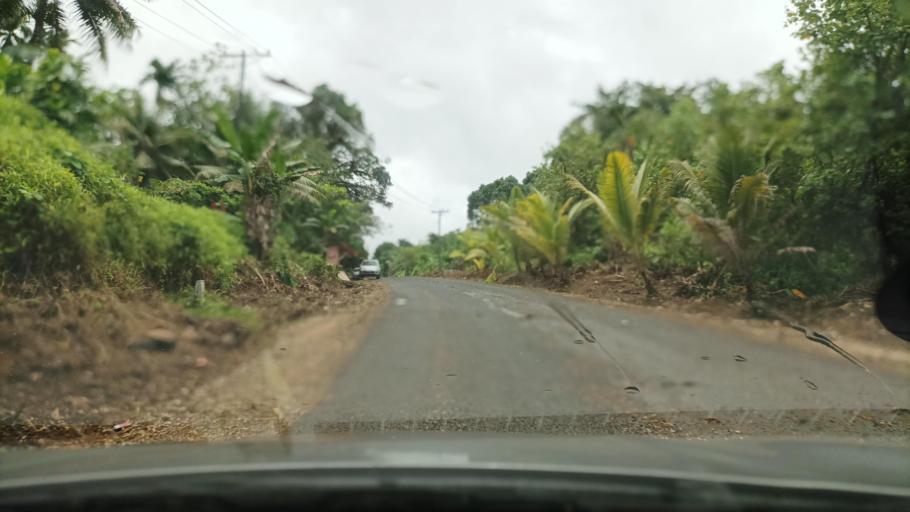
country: FM
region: Pohnpei
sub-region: Madolenihm Municipality
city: Madolenihm Municipality Government
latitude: 6.8146
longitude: 158.2360
